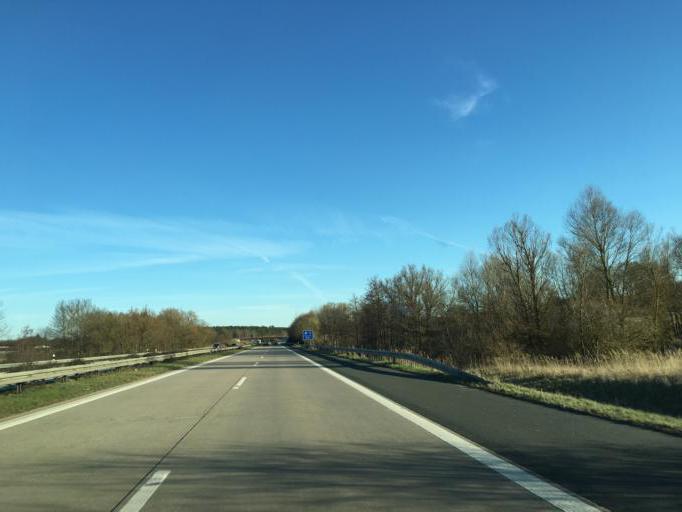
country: DE
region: Mecklenburg-Vorpommern
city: Lalendorf
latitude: 53.7884
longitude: 12.3074
